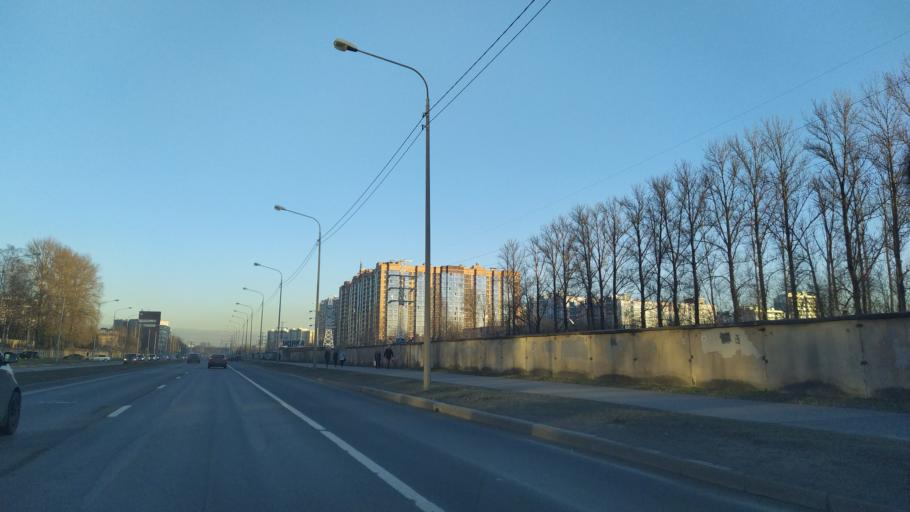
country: RU
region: St.-Petersburg
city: Kushelevka
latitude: 59.9840
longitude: 30.3683
